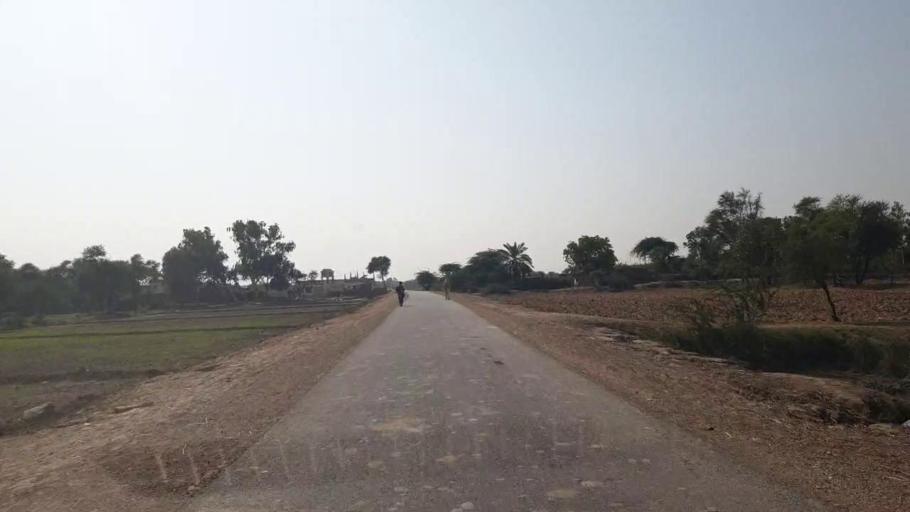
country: PK
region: Sindh
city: Matli
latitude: 24.9758
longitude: 68.6548
